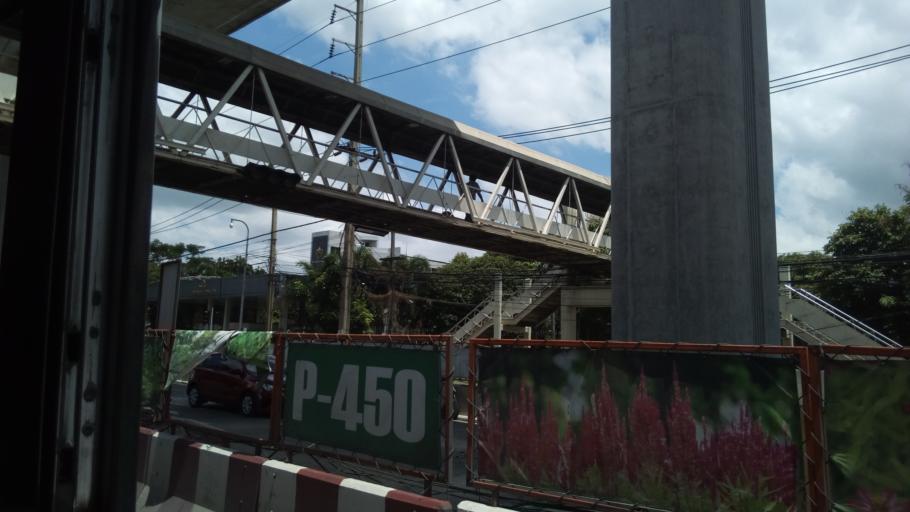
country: TH
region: Bangkok
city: Don Mueang
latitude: 13.9092
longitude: 100.6166
